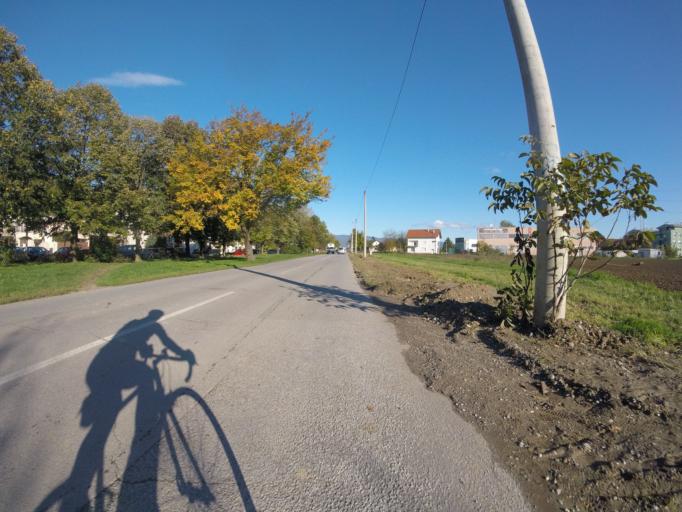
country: HR
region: Grad Zagreb
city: Odra
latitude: 45.7632
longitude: 16.0074
